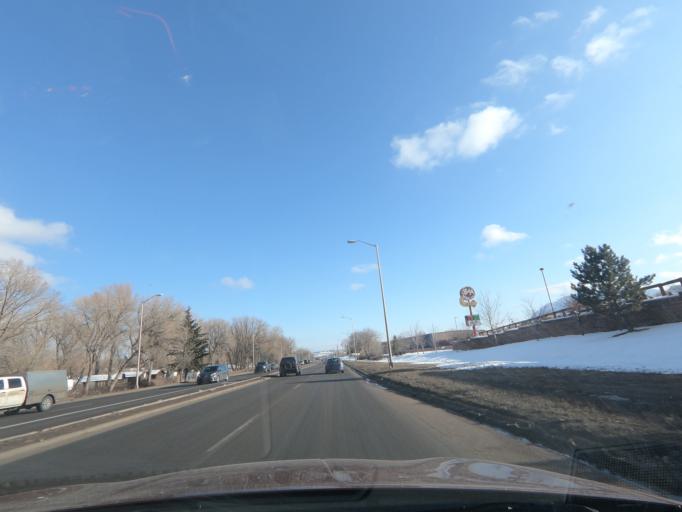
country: US
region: Colorado
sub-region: El Paso County
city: Manitou Springs
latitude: 38.8503
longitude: -104.8717
